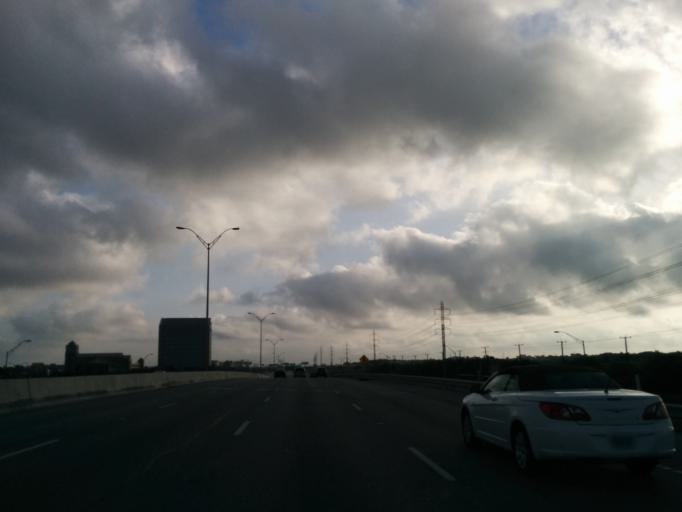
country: US
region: Texas
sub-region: Bexar County
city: Olmos Park
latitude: 29.4997
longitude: -98.4823
